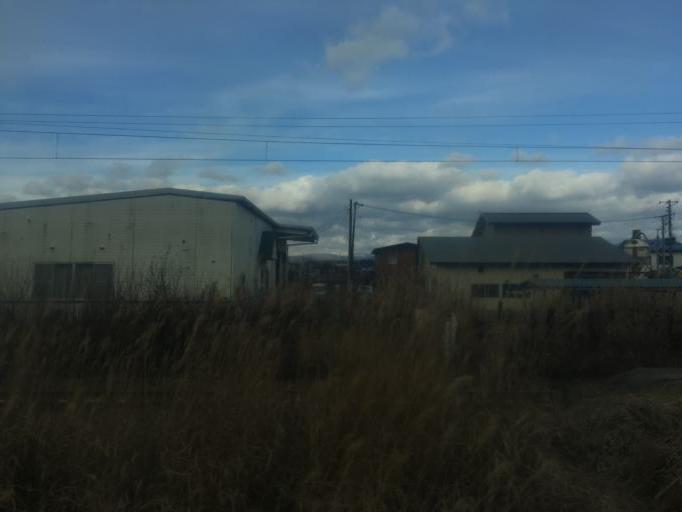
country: JP
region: Akita
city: Noshiromachi
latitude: 40.2177
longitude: 140.1720
